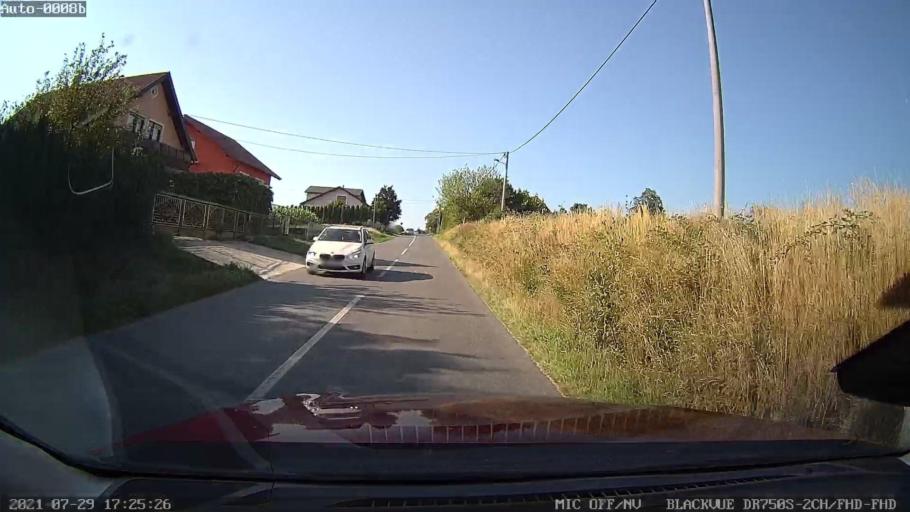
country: HR
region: Varazdinska
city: Ivanec
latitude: 46.2475
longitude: 16.1185
